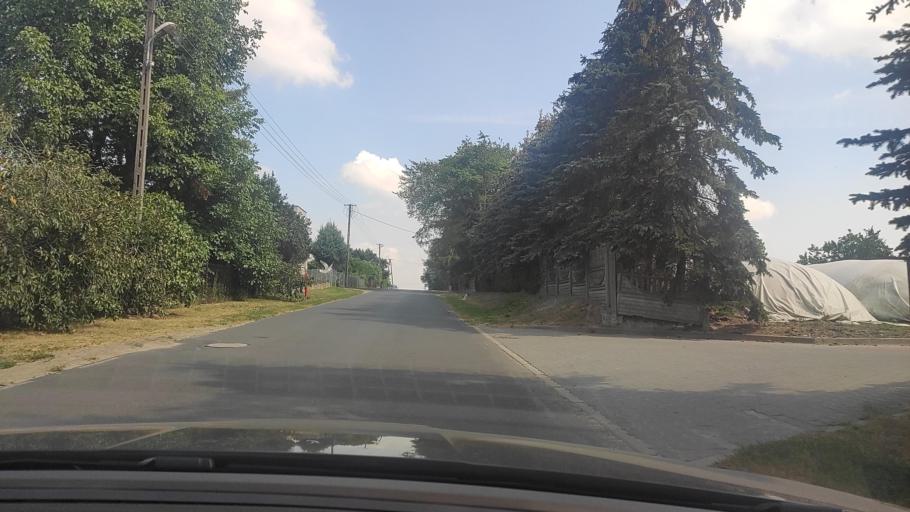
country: PL
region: Greater Poland Voivodeship
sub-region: Powiat poznanski
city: Kostrzyn
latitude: 52.4798
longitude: 17.1878
